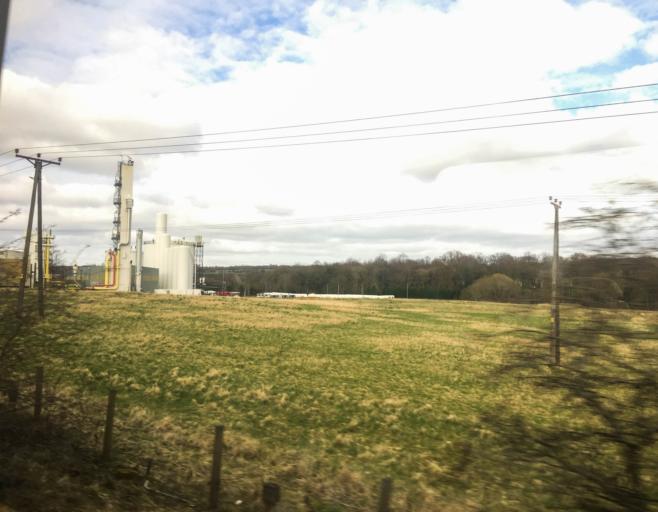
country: GB
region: Scotland
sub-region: North Lanarkshire
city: Newarthill
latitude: 55.7991
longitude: -3.9531
